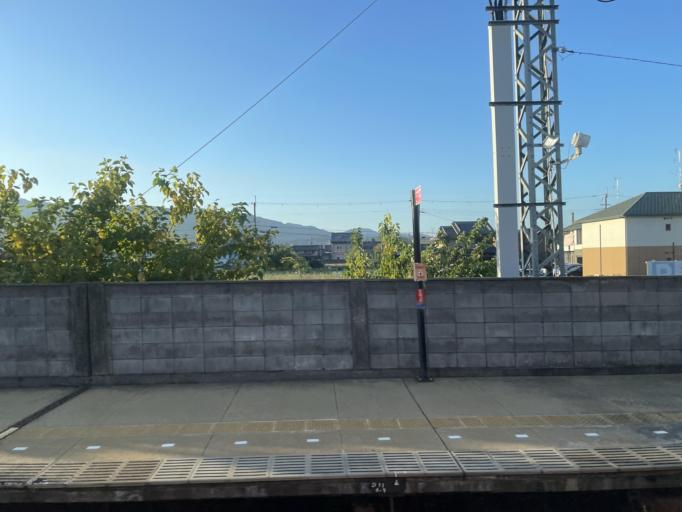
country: JP
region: Nara
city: Sakurai
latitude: 34.5129
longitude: 135.8302
